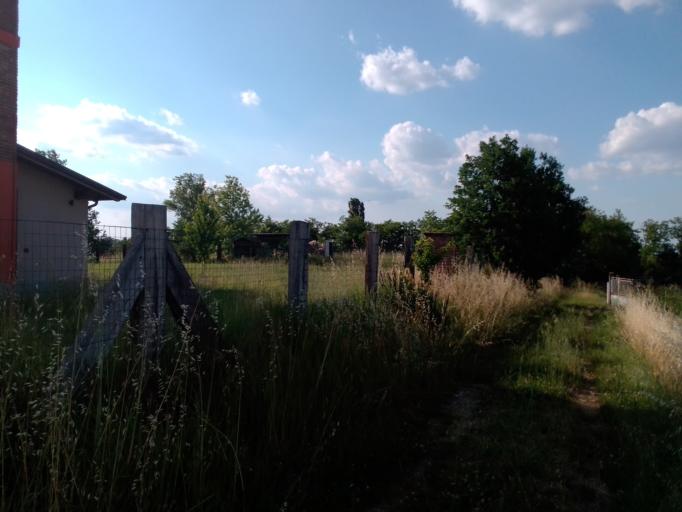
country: IT
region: Emilia-Romagna
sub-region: Provincia di Piacenza
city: Borgonovo Valtidone
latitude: 45.0083
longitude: 9.4376
